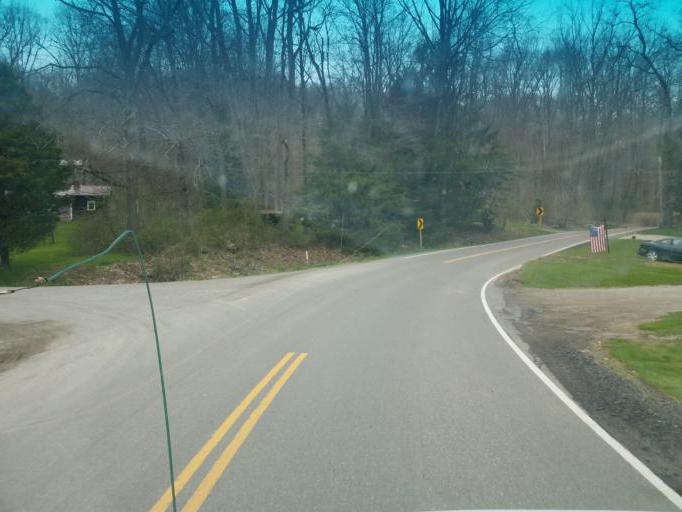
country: US
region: Ohio
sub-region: Stark County
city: Beach City
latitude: 40.6052
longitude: -81.6710
